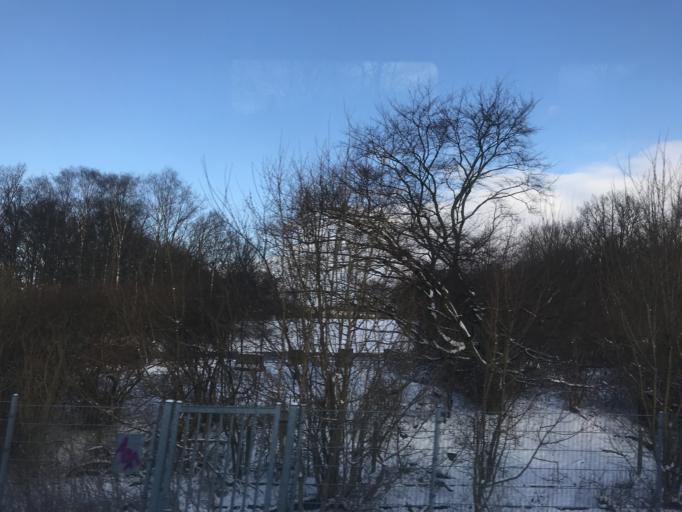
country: SE
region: Skane
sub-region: Lunds Kommun
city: Lund
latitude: 55.6966
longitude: 13.1751
